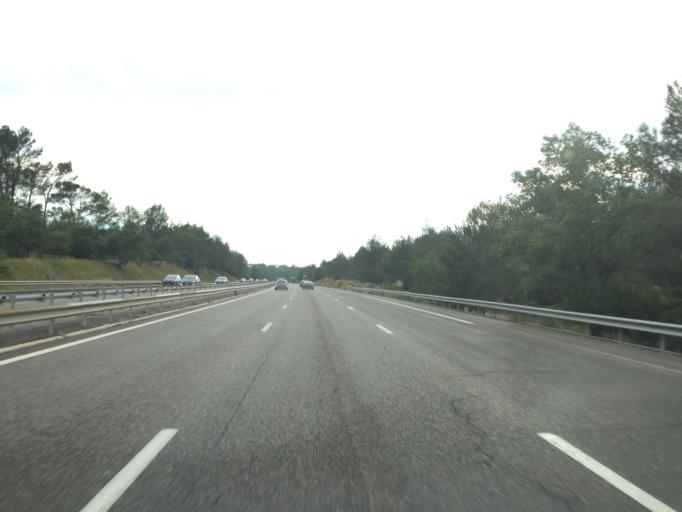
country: FR
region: Provence-Alpes-Cote d'Azur
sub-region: Departement du Var
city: Bras
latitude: 43.4249
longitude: 5.9737
